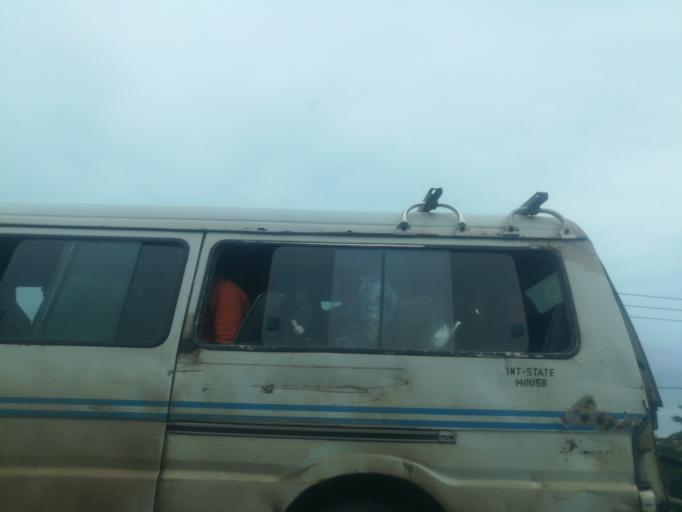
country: NG
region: Oyo
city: Ibadan
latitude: 7.3479
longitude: 3.9195
